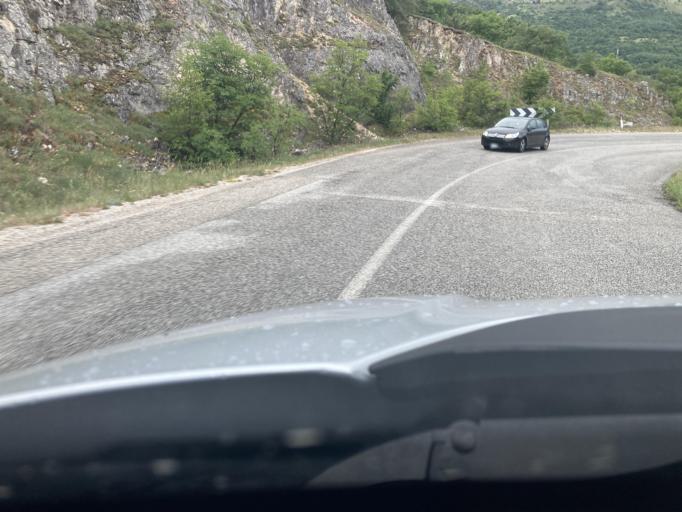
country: IT
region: Abruzzo
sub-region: Provincia dell' Aquila
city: San Panfilo d'Ocre
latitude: 42.2723
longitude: 13.4859
